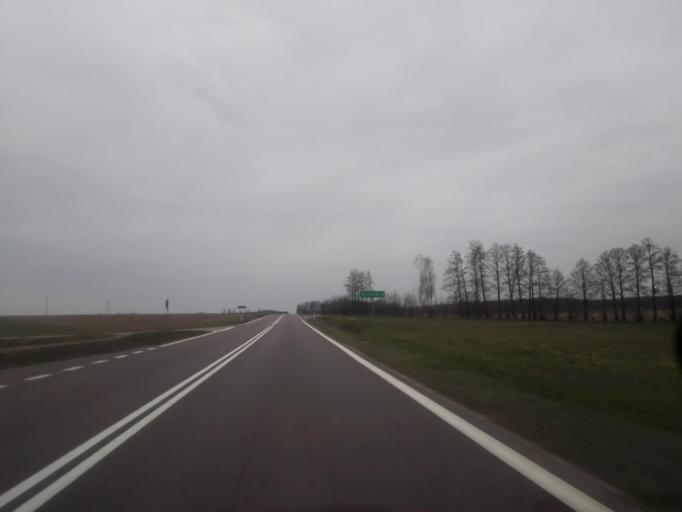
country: PL
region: Podlasie
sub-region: Powiat grajewski
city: Szczuczyn
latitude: 53.5335
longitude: 22.2604
